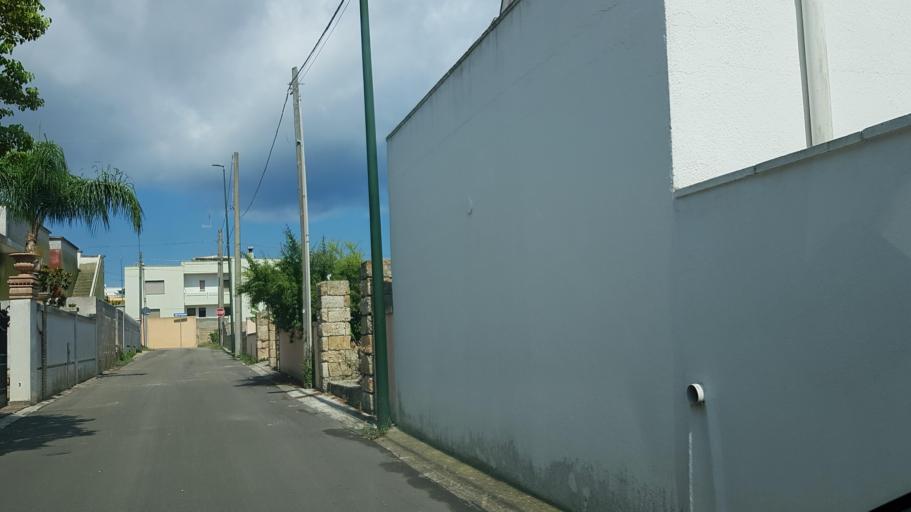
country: IT
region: Apulia
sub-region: Provincia di Lecce
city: Castrignano del Capo
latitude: 39.8294
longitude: 18.3527
